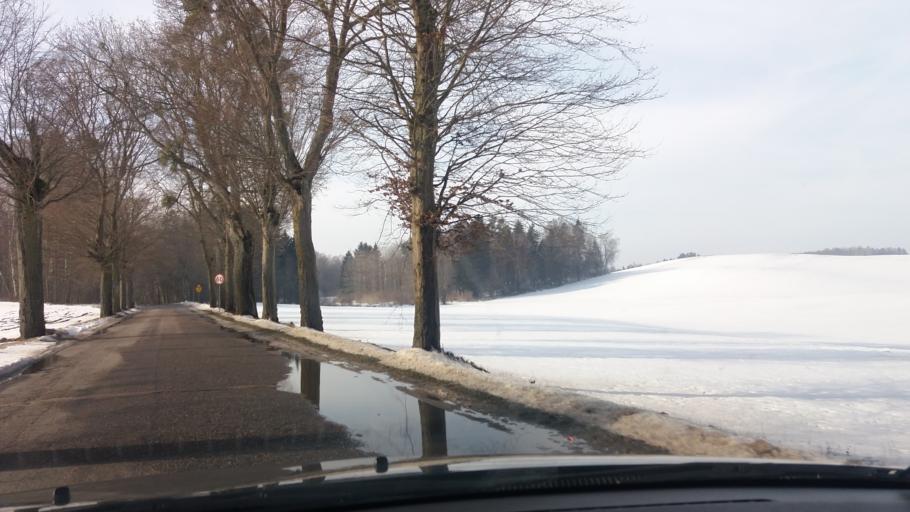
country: PL
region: Warmian-Masurian Voivodeship
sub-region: Powiat lidzbarski
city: Lidzbark Warminski
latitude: 54.1075
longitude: 20.6441
